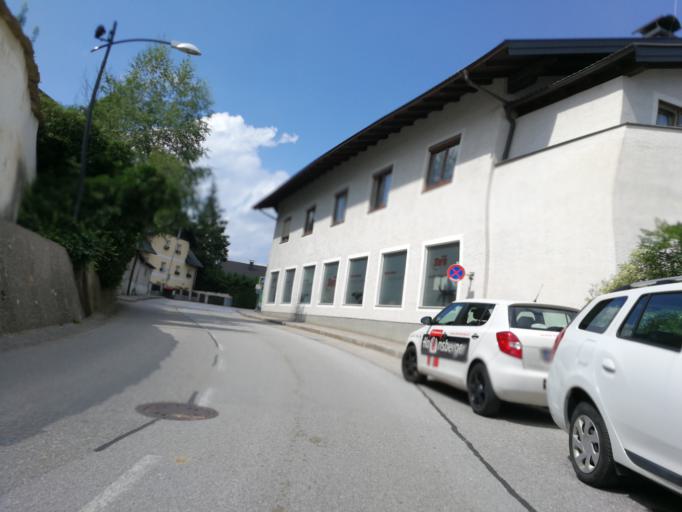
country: AT
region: Salzburg
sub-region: Politischer Bezirk Salzburg-Umgebung
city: Bergheim
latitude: 47.8241
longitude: 13.0095
